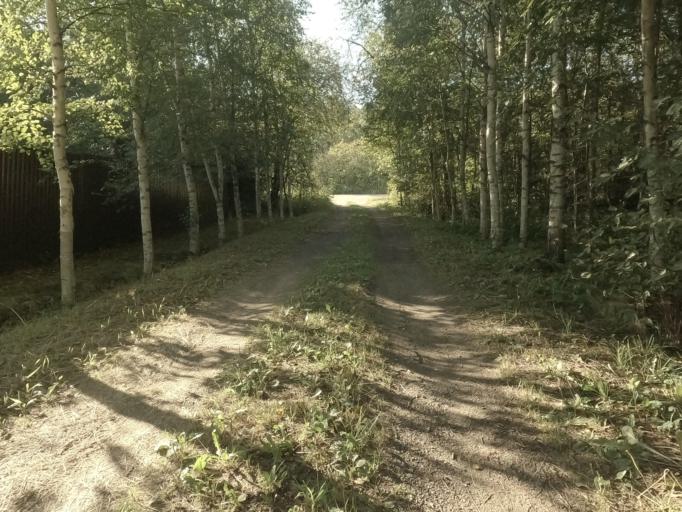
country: RU
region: Leningrad
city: Kirovsk
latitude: 59.9251
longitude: 30.9747
